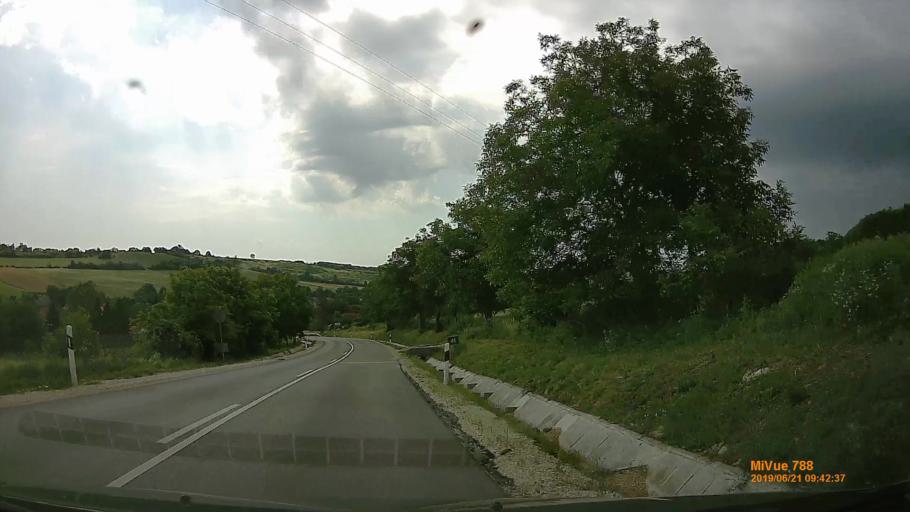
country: HU
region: Somogy
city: Taszar
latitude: 46.2871
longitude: 17.9689
